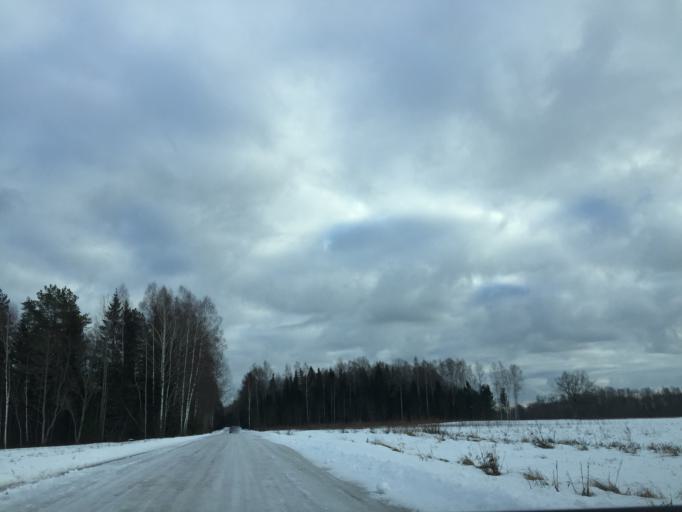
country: LV
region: Lielvarde
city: Lielvarde
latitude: 56.5840
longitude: 24.7401
